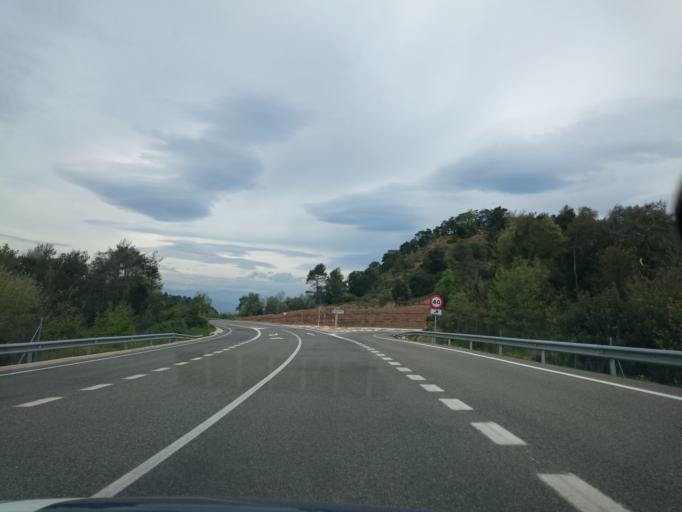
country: ES
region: Catalonia
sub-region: Provincia de Barcelona
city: Olost
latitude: 41.9569
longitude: 2.1356
